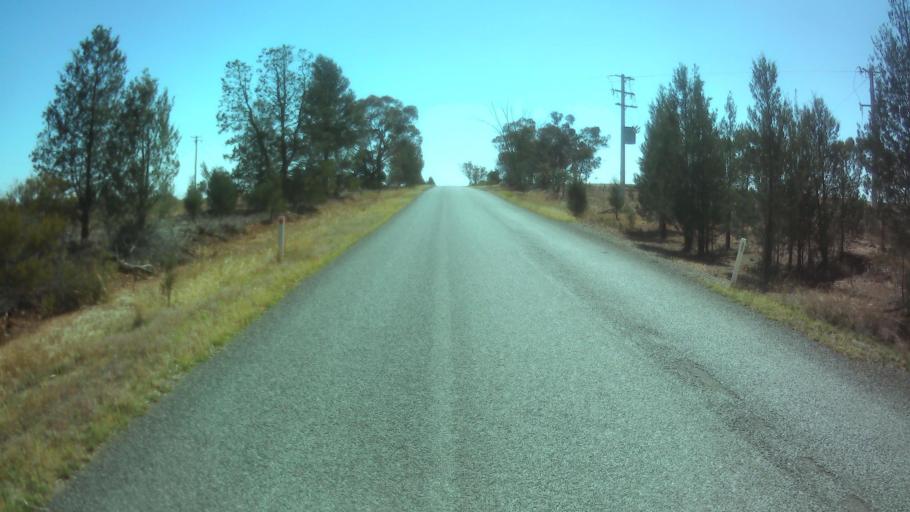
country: AU
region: New South Wales
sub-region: Weddin
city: Grenfell
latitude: -33.7535
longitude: 147.8404
